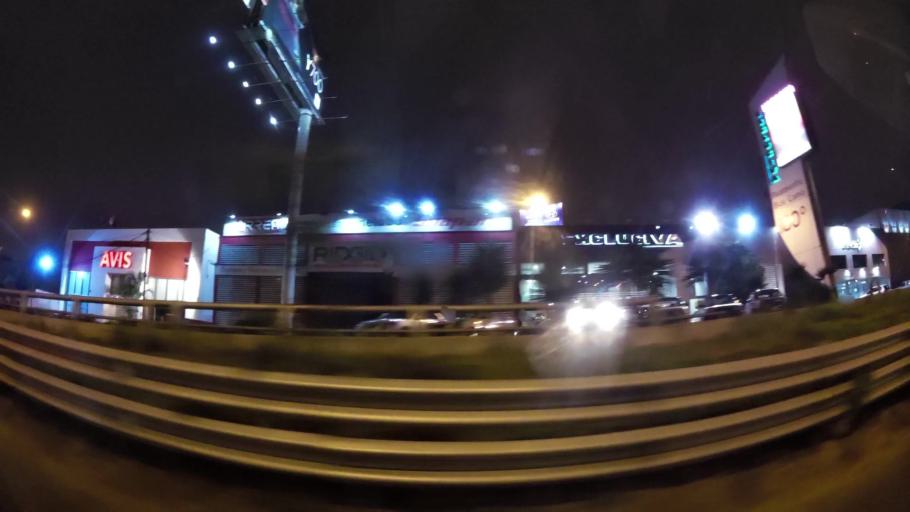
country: PE
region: Lima
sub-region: Lima
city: San Luis
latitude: -12.0897
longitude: -77.0160
